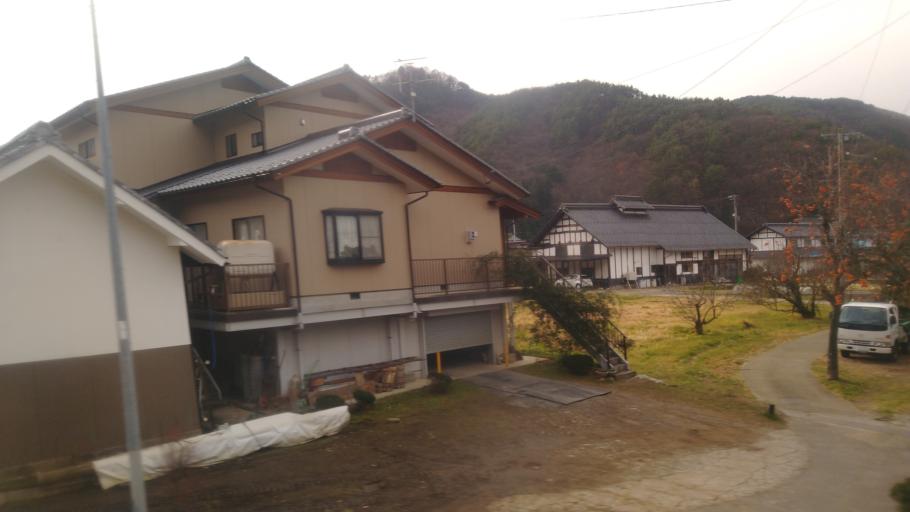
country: JP
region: Nagano
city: Omachi
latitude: 36.4516
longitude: 138.0649
